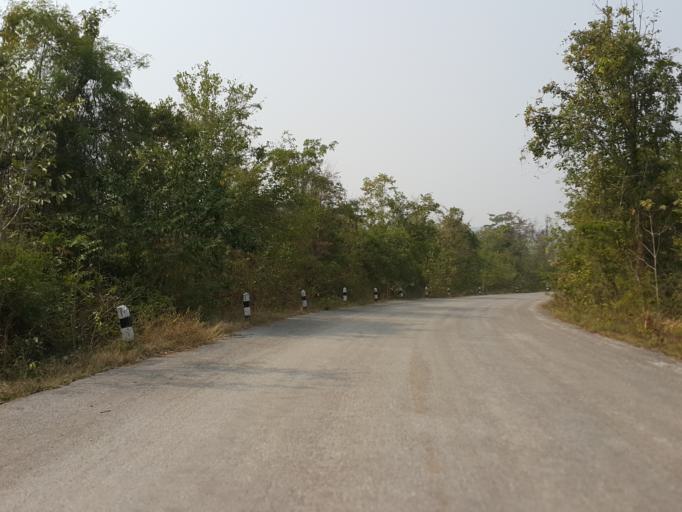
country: TH
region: Lampang
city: Mae Phrik
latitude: 17.4947
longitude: 99.0864
